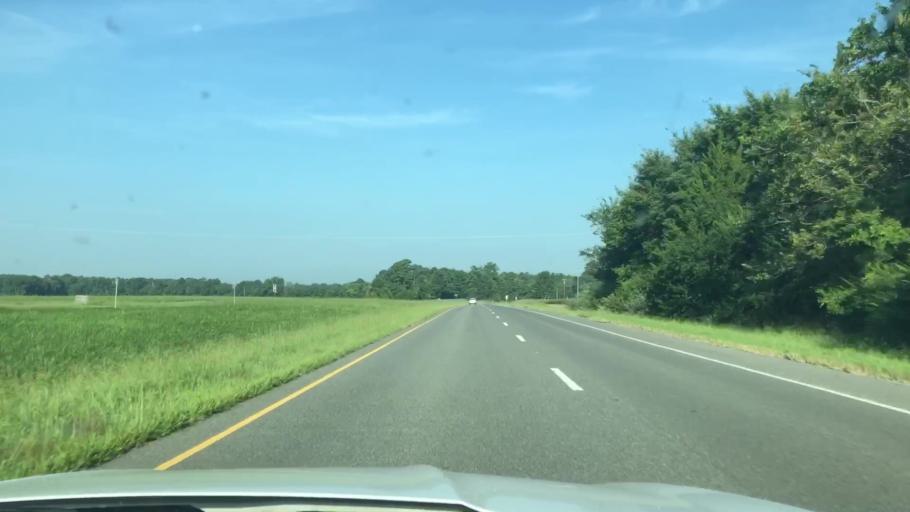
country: US
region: Virginia
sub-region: King and Queen County
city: King and Queen Court House
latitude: 37.7687
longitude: -76.7403
